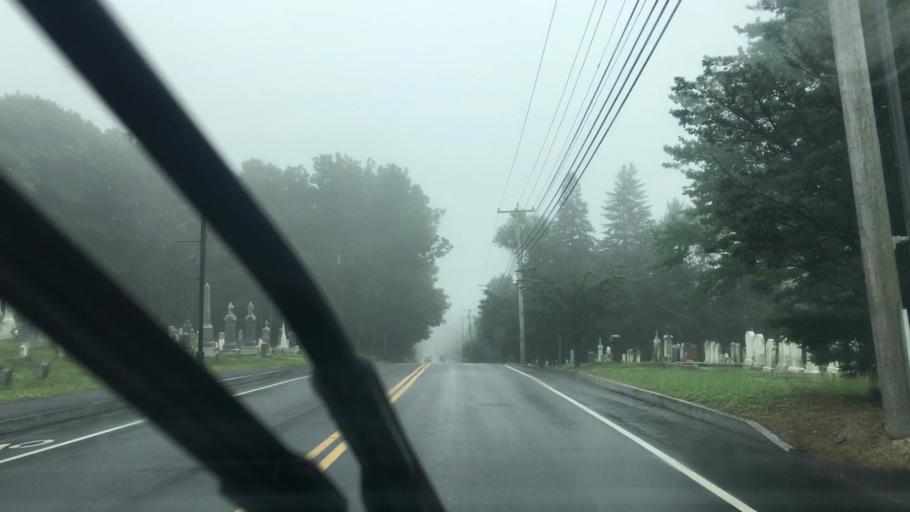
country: US
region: Maine
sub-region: Lincoln County
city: Boothbay
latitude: 43.8742
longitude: -69.6333
